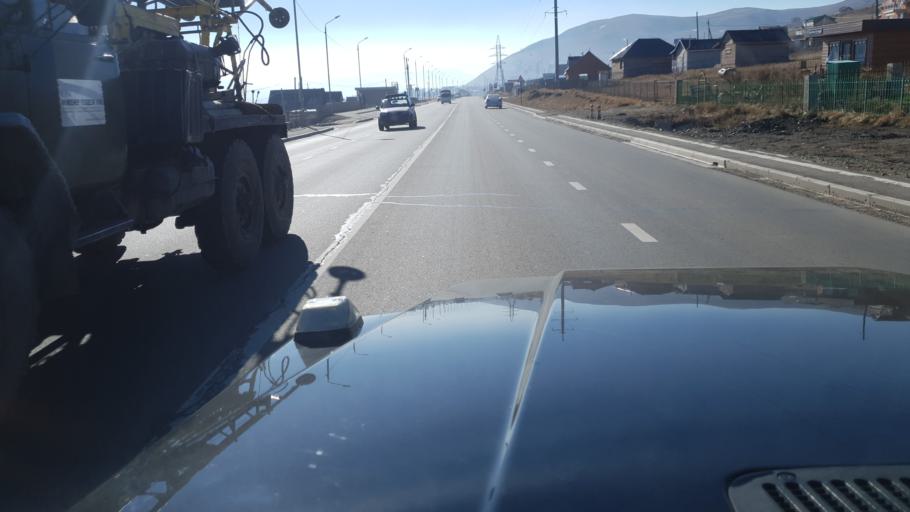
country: MN
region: Ulaanbaatar
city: Ulaanbaatar
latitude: 48.0265
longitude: 106.9127
